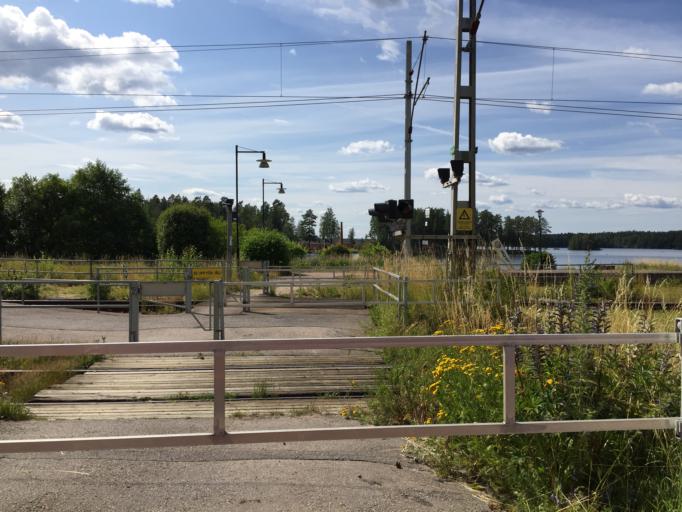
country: SE
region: Vaestmanland
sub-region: Norbergs Kommun
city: Norberg
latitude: 59.9576
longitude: 16.0096
